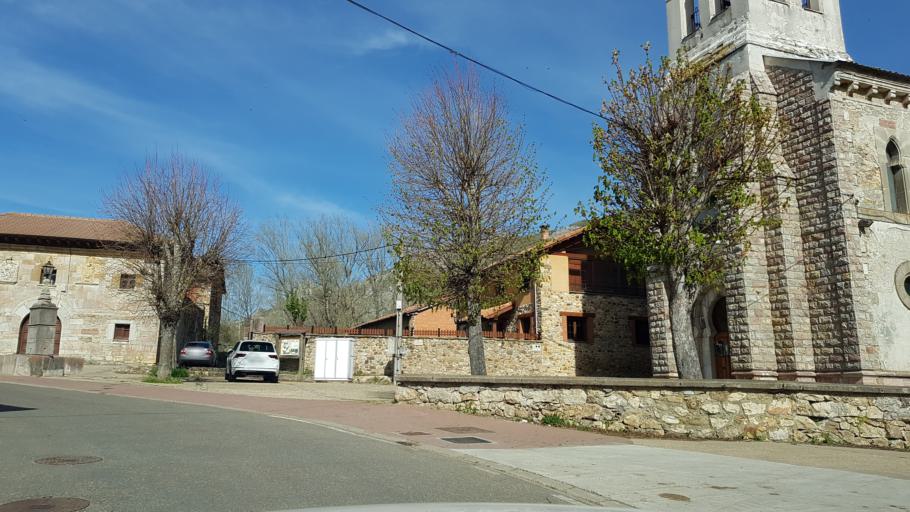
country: ES
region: Castille and Leon
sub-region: Provincia de Leon
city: Carmenes
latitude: 42.9592
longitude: -5.5725
